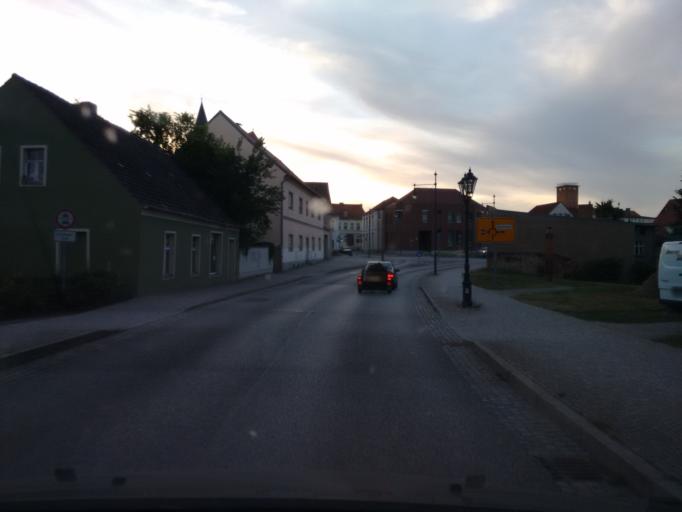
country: DE
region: Brandenburg
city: Beeskow
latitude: 52.1705
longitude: 14.2508
